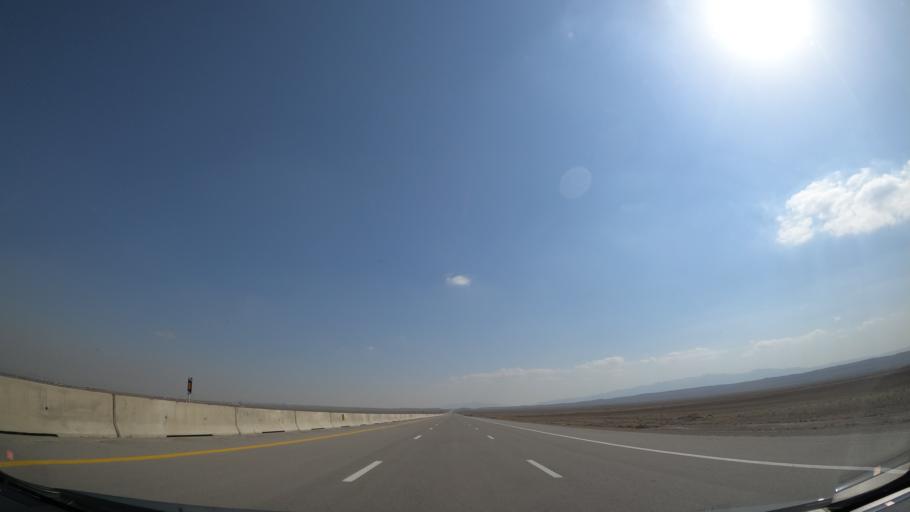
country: IR
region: Alborz
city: Nazarabad
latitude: 35.8337
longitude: 50.4963
